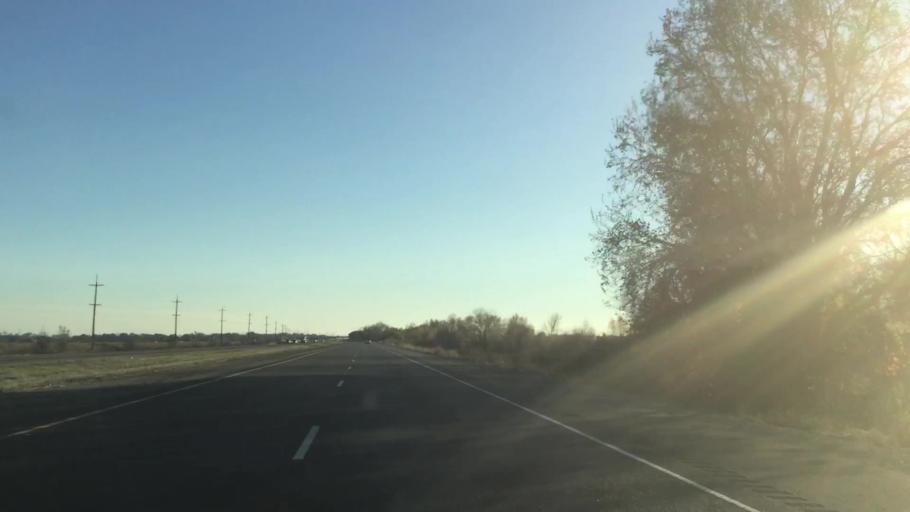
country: US
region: California
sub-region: Yuba County
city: Plumas Lake
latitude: 38.9948
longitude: -121.5436
